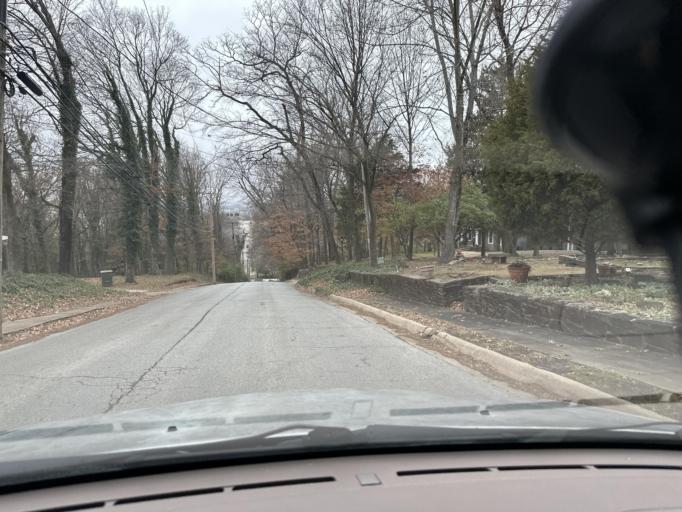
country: US
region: Arkansas
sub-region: Washington County
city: Fayetteville
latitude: 36.0646
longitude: -94.1521
